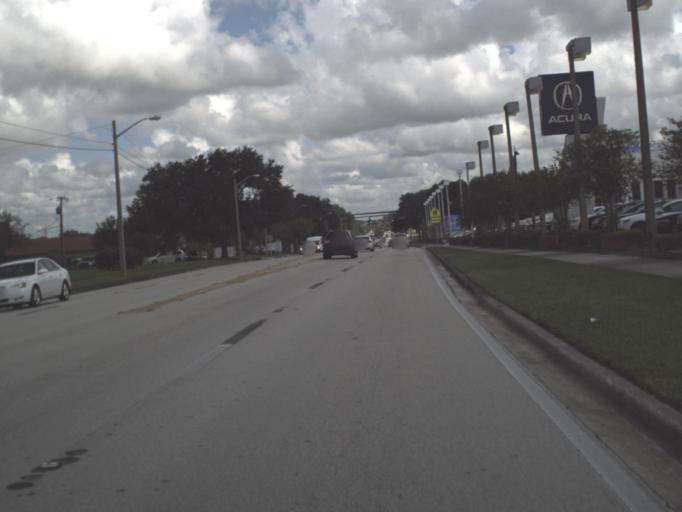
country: US
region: Florida
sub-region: Polk County
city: Lakeland
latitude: 28.0751
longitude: -81.9532
